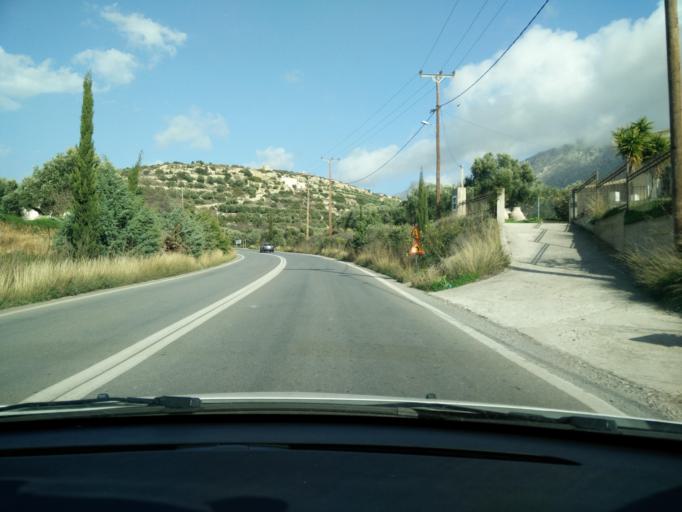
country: GR
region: Crete
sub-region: Nomos Lasithiou
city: Kato Chorio
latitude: 35.0585
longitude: 25.7982
